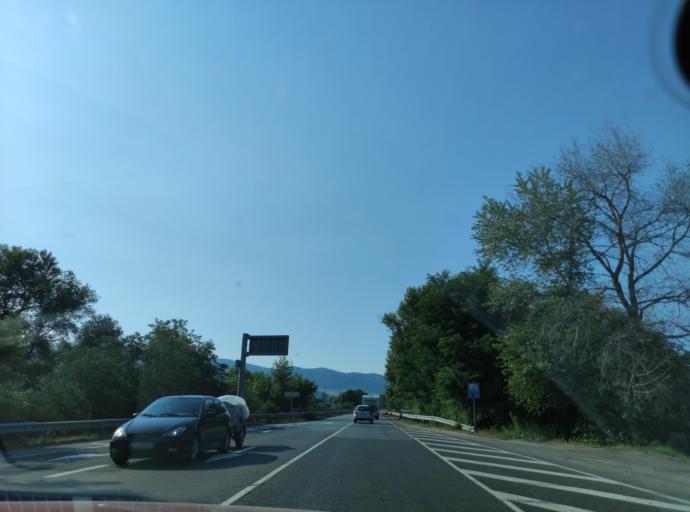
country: BG
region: Blagoevgrad
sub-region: Obshtina Simitli
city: Simitli
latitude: 41.8541
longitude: 23.1363
